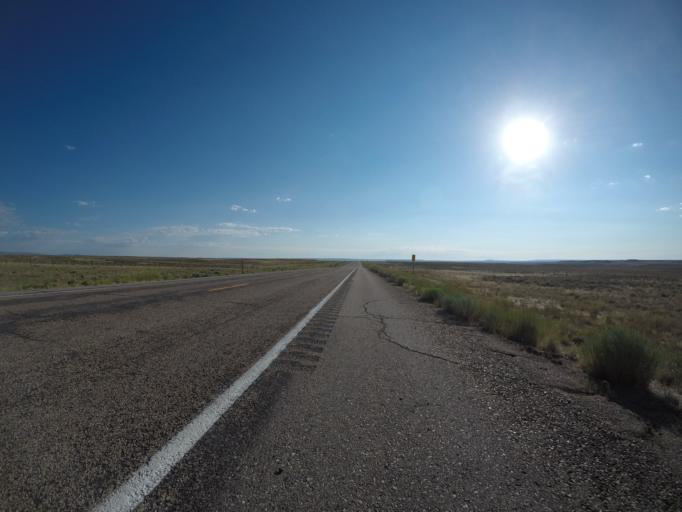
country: US
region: Wyoming
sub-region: Lincoln County
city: Kemmerer
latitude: 41.9272
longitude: -110.2807
